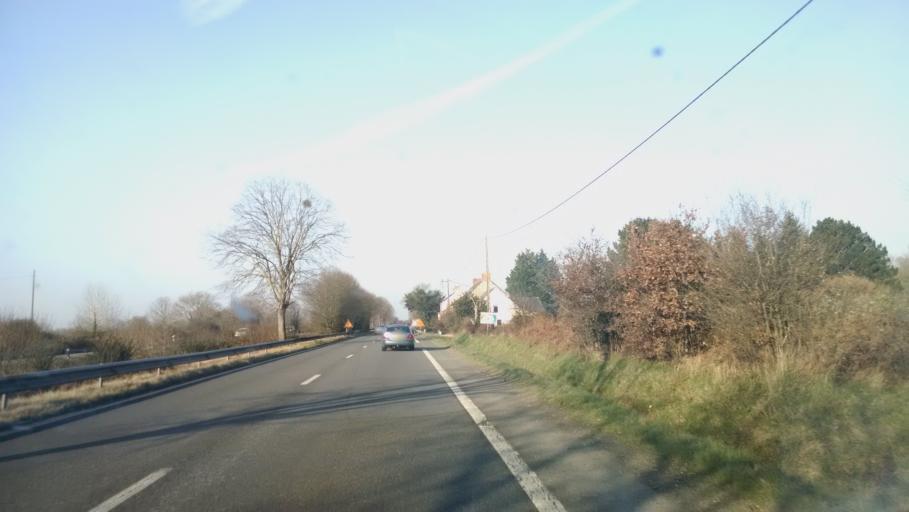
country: FR
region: Pays de la Loire
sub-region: Departement de la Loire-Atlantique
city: Malville
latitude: 47.3444
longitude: -1.8529
